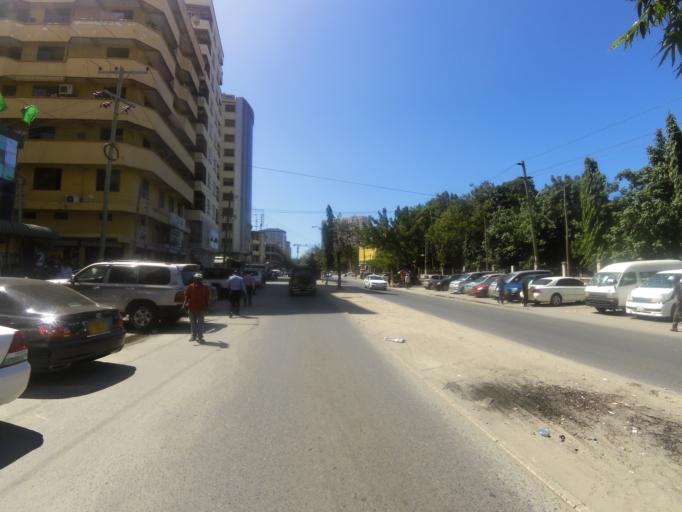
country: TZ
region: Dar es Salaam
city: Dar es Salaam
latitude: -6.8183
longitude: 39.2788
